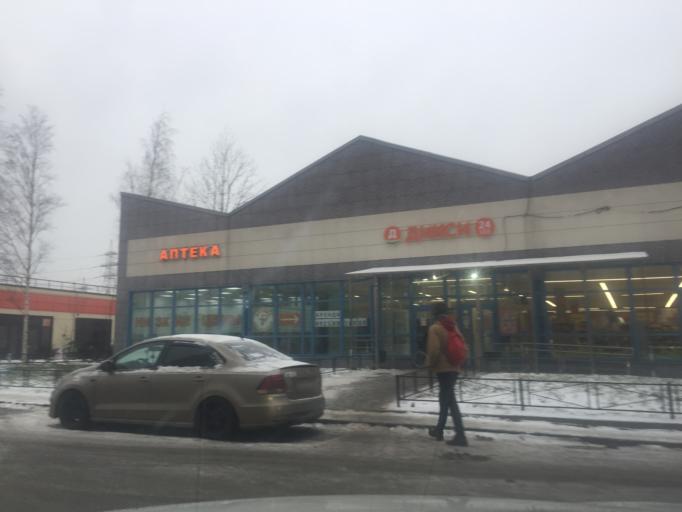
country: RU
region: Leningrad
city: Murino
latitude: 60.0420
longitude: 30.4468
